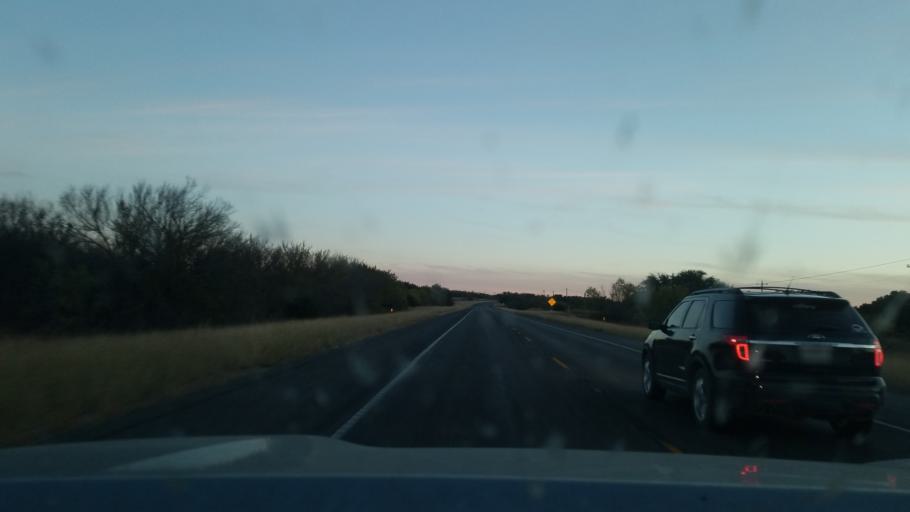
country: US
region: Texas
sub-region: Stephens County
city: Breckenridge
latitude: 32.5819
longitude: -98.8966
